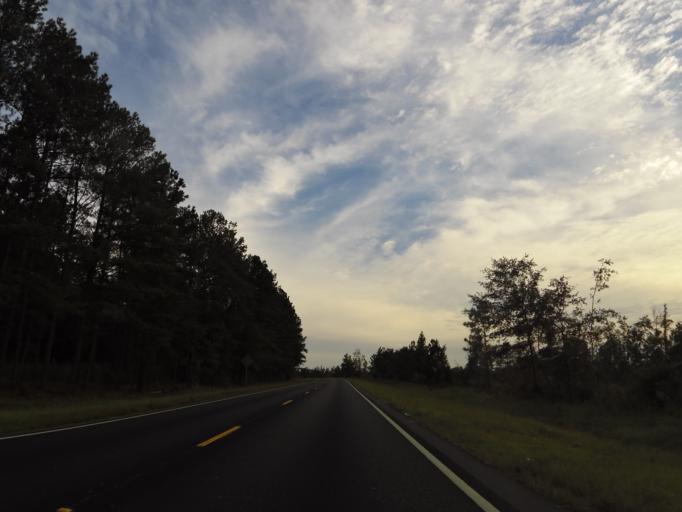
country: US
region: Alabama
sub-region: Monroe County
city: Frisco City
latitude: 31.2528
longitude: -87.4924
